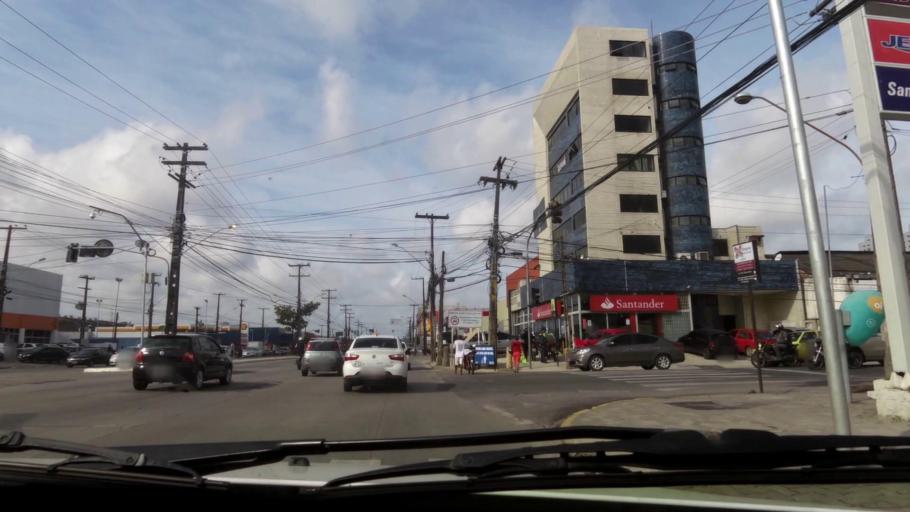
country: BR
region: Pernambuco
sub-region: Recife
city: Recife
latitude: -8.1079
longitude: -34.9116
